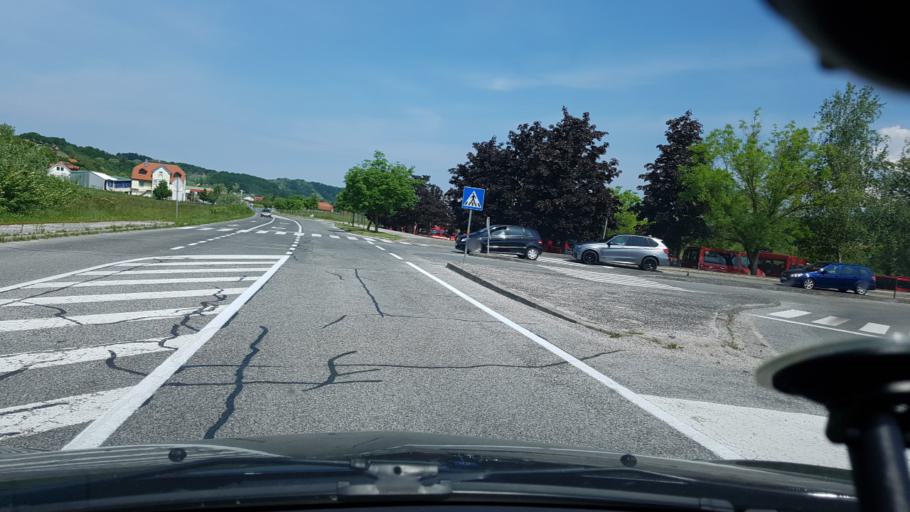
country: HR
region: Krapinsko-Zagorska
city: Marija Bistrica
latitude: 46.0000
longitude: 16.1164
